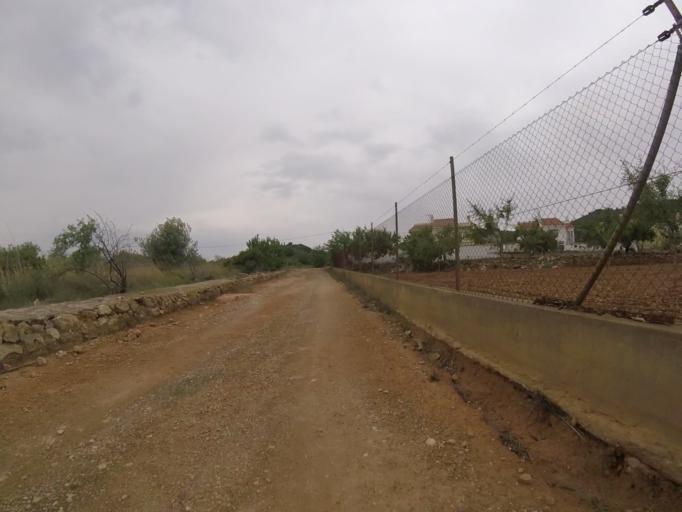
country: ES
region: Valencia
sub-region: Provincia de Castello
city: Alcoceber
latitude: 40.2460
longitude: 0.2562
